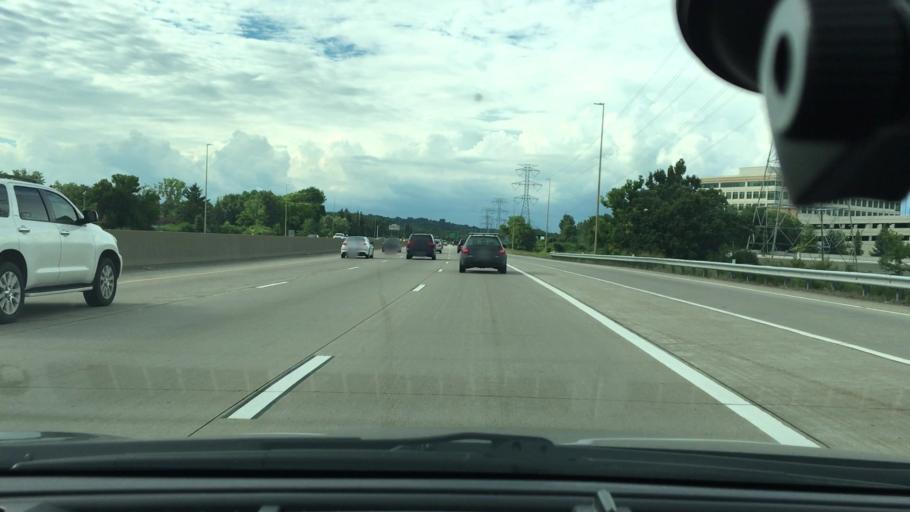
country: US
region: Minnesota
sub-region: Hennepin County
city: Hopkins
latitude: 44.8956
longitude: -93.4442
